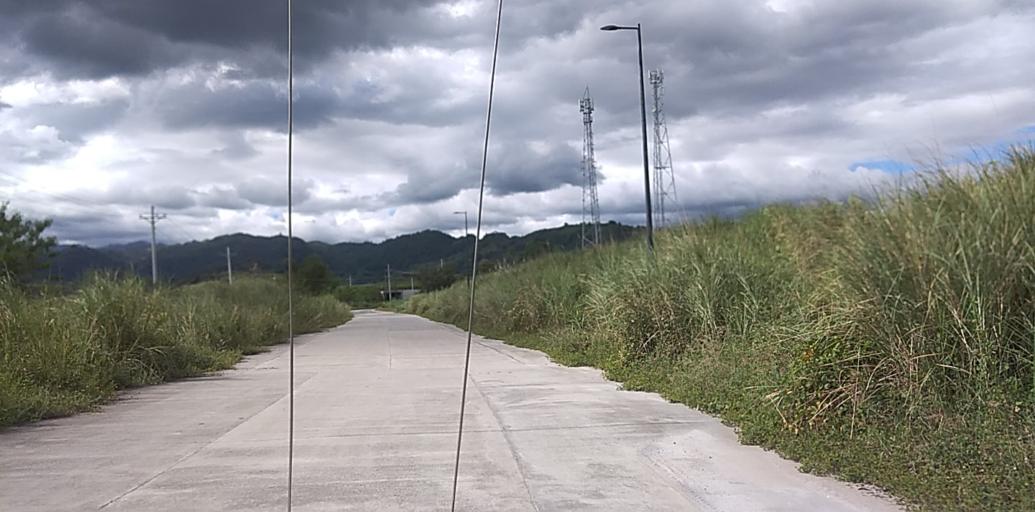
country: PH
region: Central Luzon
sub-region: Province of Pampanga
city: Dolores
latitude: 15.1150
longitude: 120.5076
